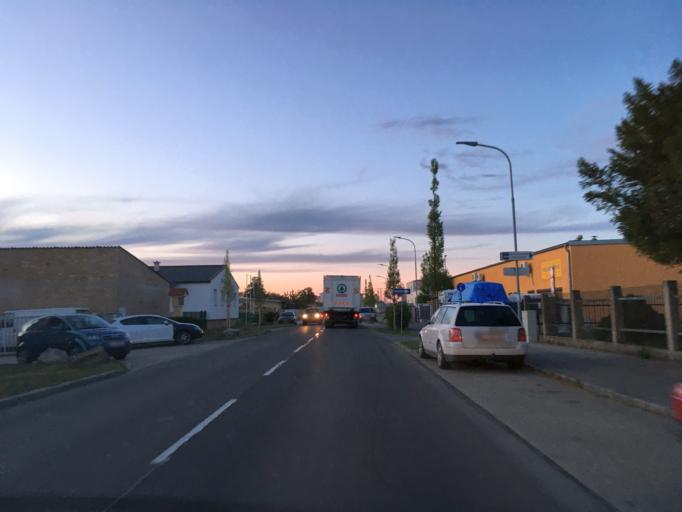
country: AT
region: Lower Austria
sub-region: Politischer Bezirk Wien-Umgebung
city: Zwolfaxing
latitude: 48.1190
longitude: 16.4684
